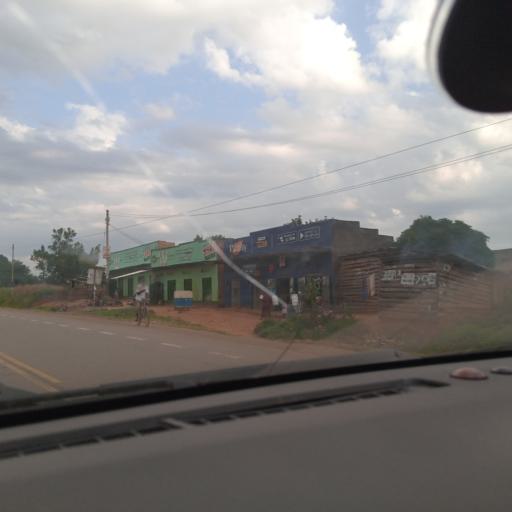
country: UG
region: Central Region
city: Masaka
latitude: -0.3370
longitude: 31.6917
